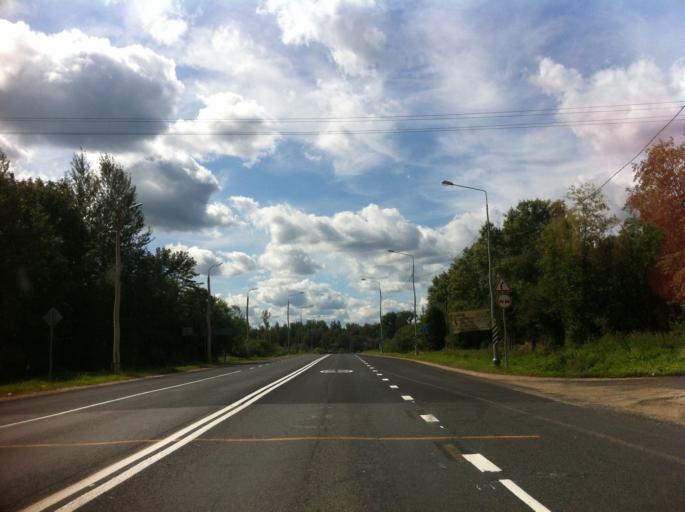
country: RU
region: Pskov
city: Izborsk
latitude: 57.7064
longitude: 27.8793
